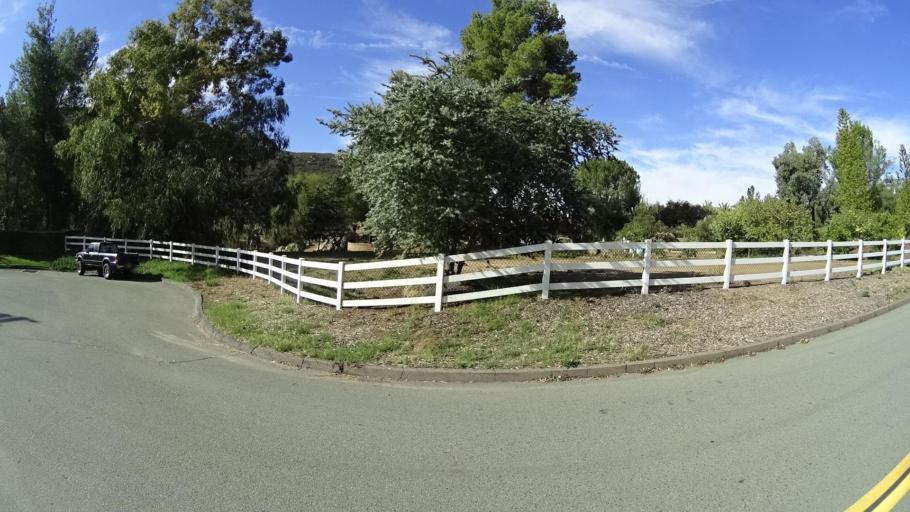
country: US
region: California
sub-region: San Diego County
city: Alpine
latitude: 32.8136
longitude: -116.7204
